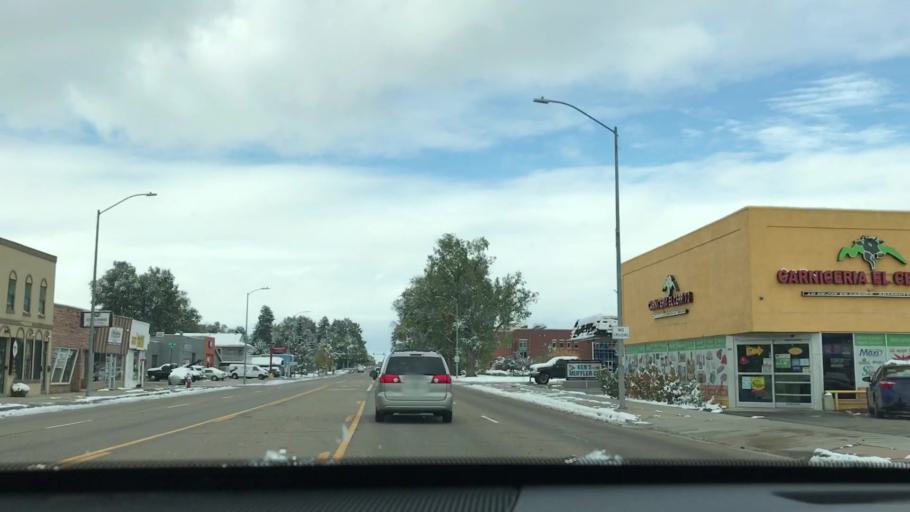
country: US
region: Colorado
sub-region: Boulder County
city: Longmont
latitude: 40.1751
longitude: -105.1025
